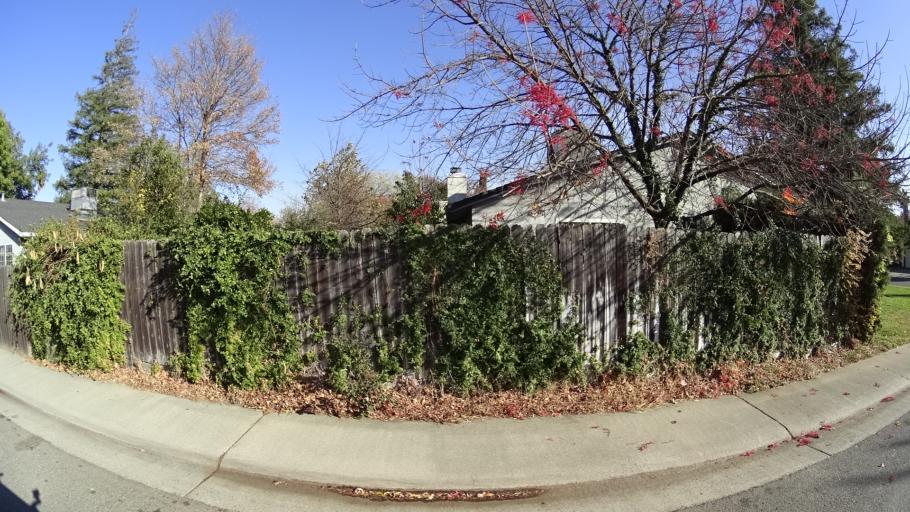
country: US
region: California
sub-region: Sacramento County
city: Antelope
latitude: 38.6944
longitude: -121.3261
